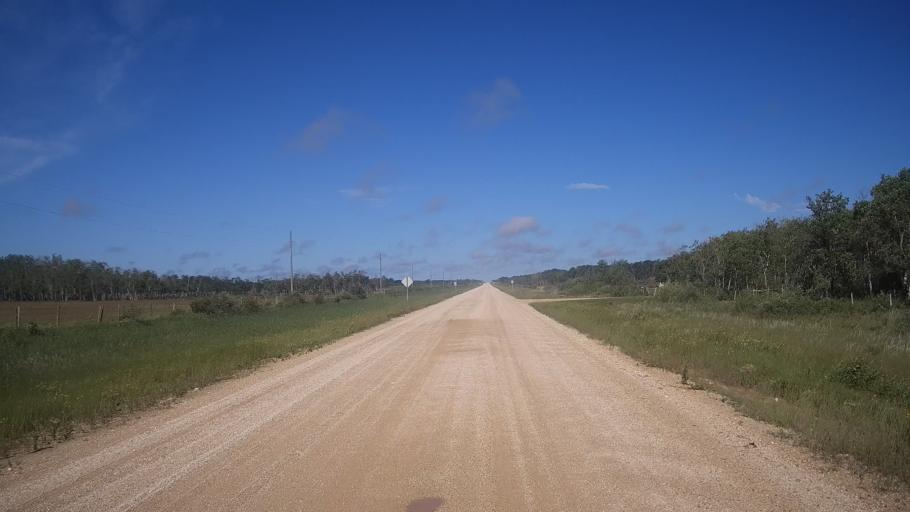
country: CA
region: Manitoba
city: Stonewall
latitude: 50.2411
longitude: -97.7175
